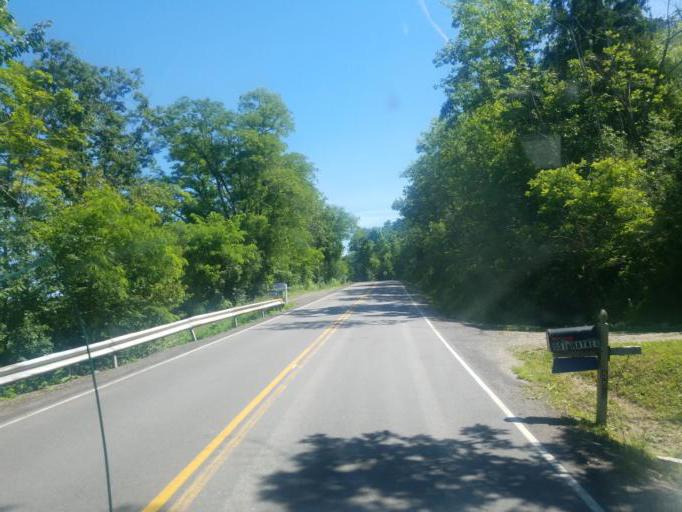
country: US
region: New York
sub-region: Ontario County
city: Canandaigua
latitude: 42.7376
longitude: -77.3229
